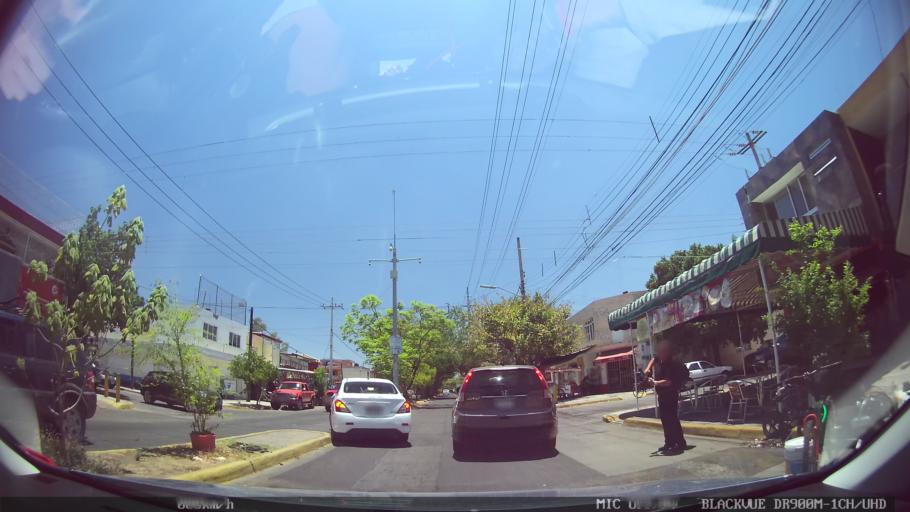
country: MX
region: Jalisco
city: Tlaquepaque
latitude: 20.6686
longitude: -103.2827
